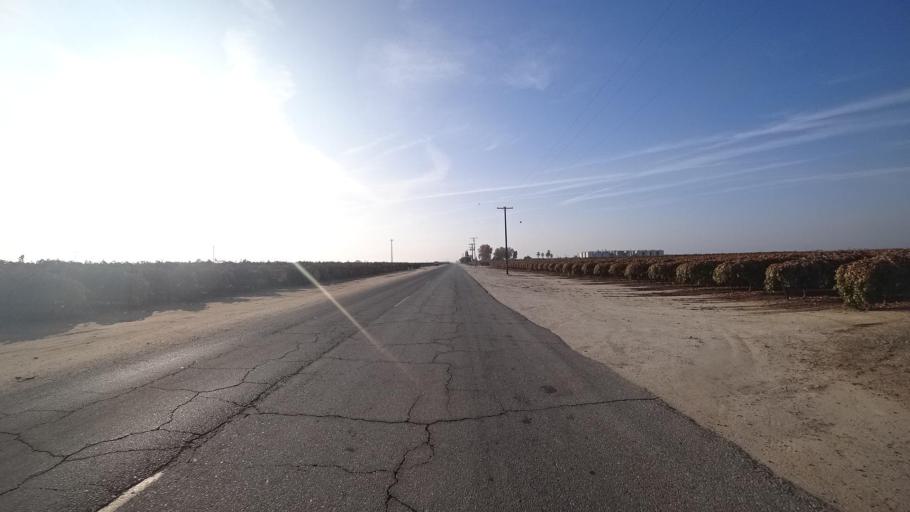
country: US
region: California
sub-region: Kern County
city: Delano
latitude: 35.7884
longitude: -119.1876
